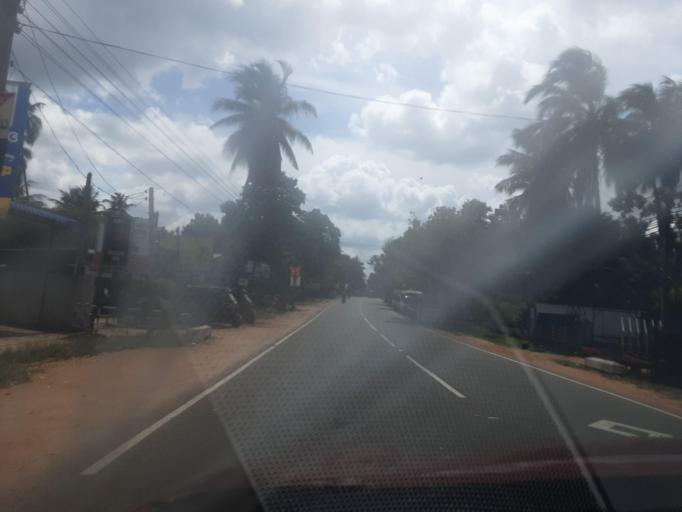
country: LK
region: North Western
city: Kuliyapitiya
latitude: 7.4693
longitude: 80.0530
